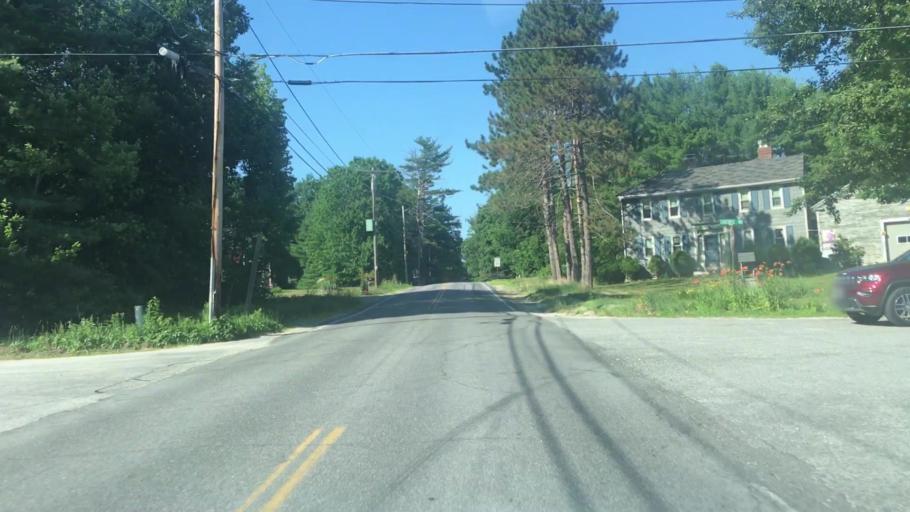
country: US
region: Maine
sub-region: York County
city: Buxton
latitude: 43.7137
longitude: -70.5701
